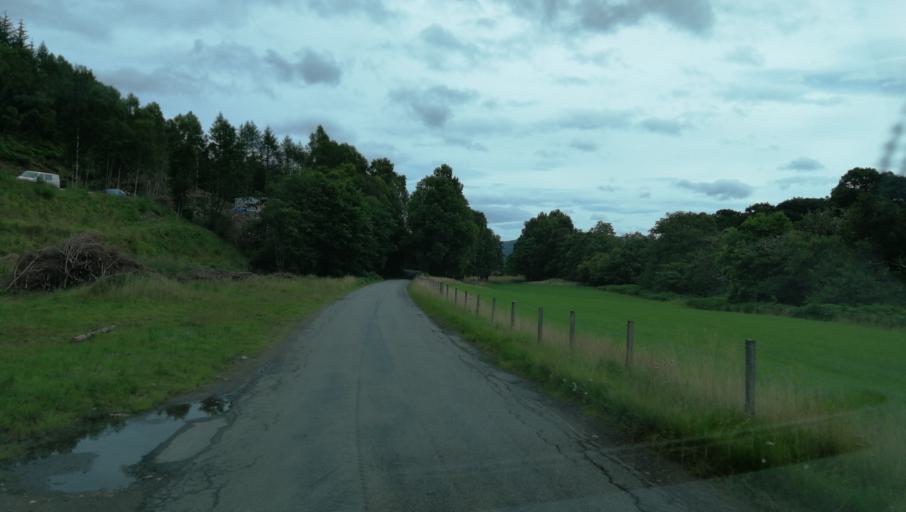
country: GB
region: Scotland
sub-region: Highland
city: Beauly
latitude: 57.3333
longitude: -4.7874
